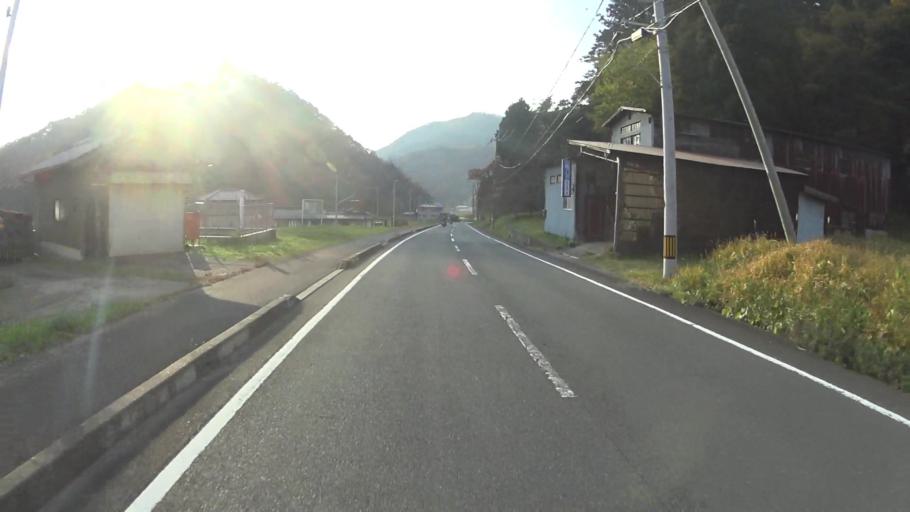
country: JP
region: Kyoto
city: Maizuru
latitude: 35.5077
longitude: 135.4440
